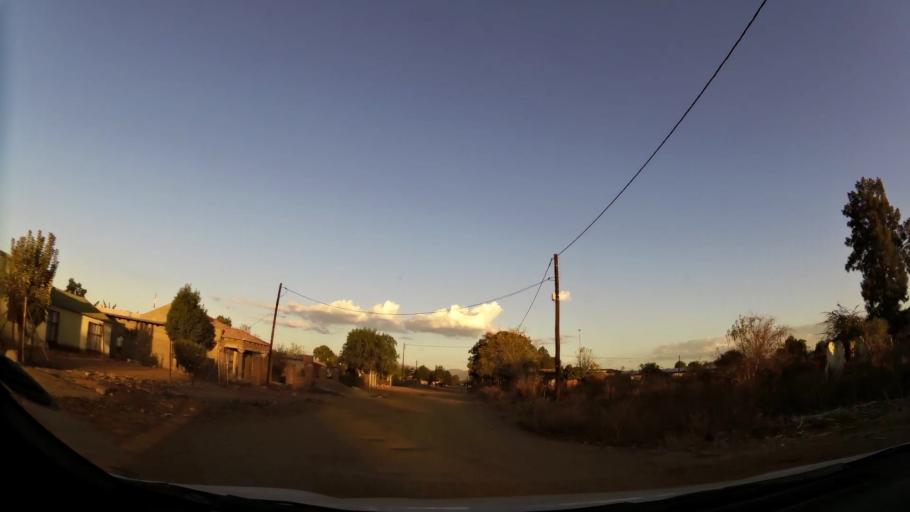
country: ZA
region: Limpopo
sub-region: Waterberg District Municipality
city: Mokopane
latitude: -24.1466
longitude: 28.9761
